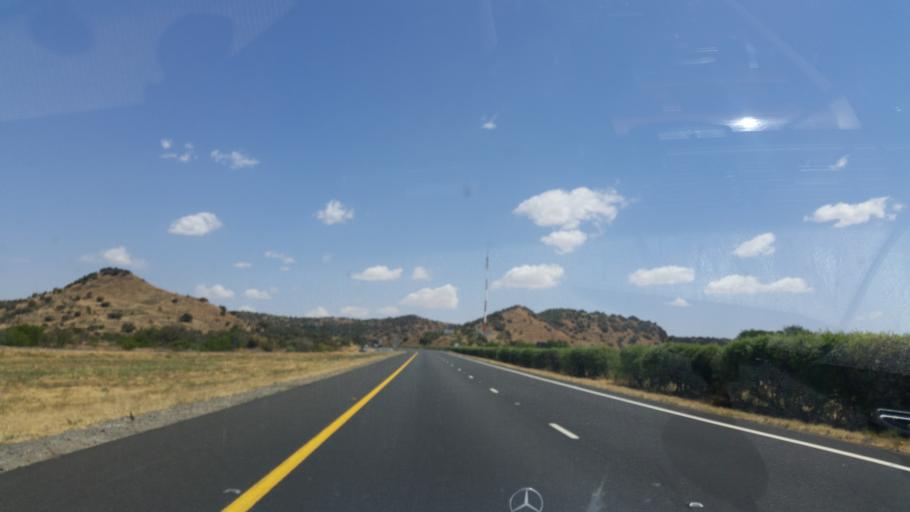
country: ZA
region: Orange Free State
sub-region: Mangaung Metropolitan Municipality
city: Bloemfontein
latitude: -28.9782
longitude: 26.2883
